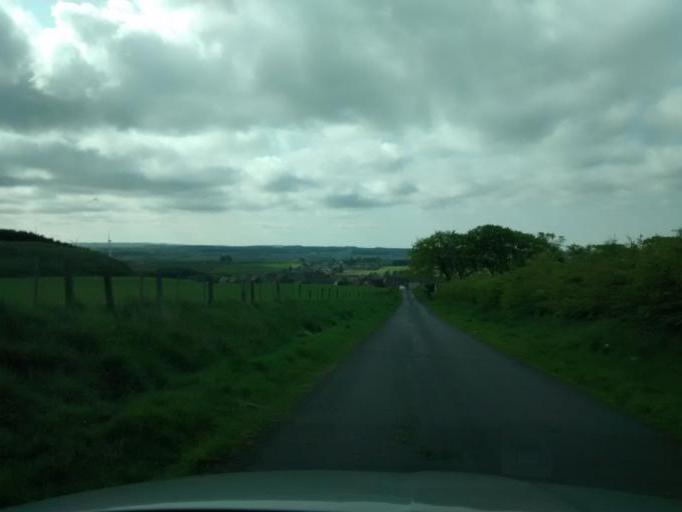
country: GB
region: Scotland
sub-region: North Lanarkshire
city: Harthill
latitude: 55.8885
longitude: -3.7667
